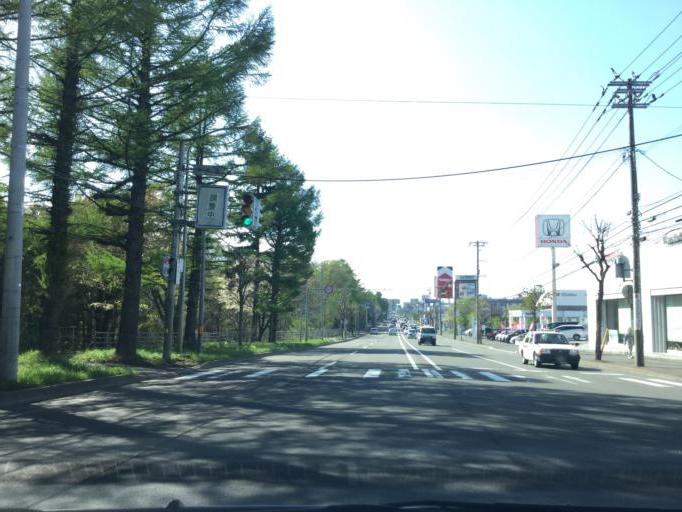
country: JP
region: Hokkaido
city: Sapporo
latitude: 43.0127
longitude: 141.4185
